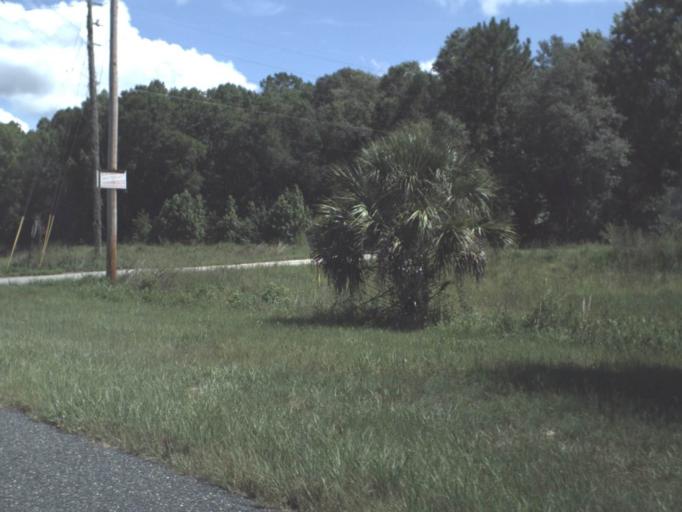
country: US
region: Florida
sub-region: Levy County
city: Inglis
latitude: 29.2222
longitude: -82.7041
